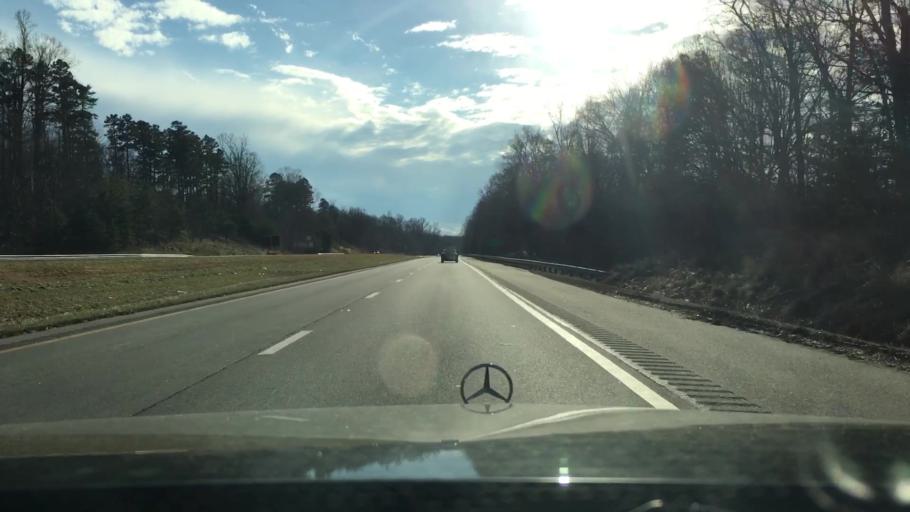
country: US
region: Virginia
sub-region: City of Danville
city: Danville
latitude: 36.5545
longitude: -79.3902
